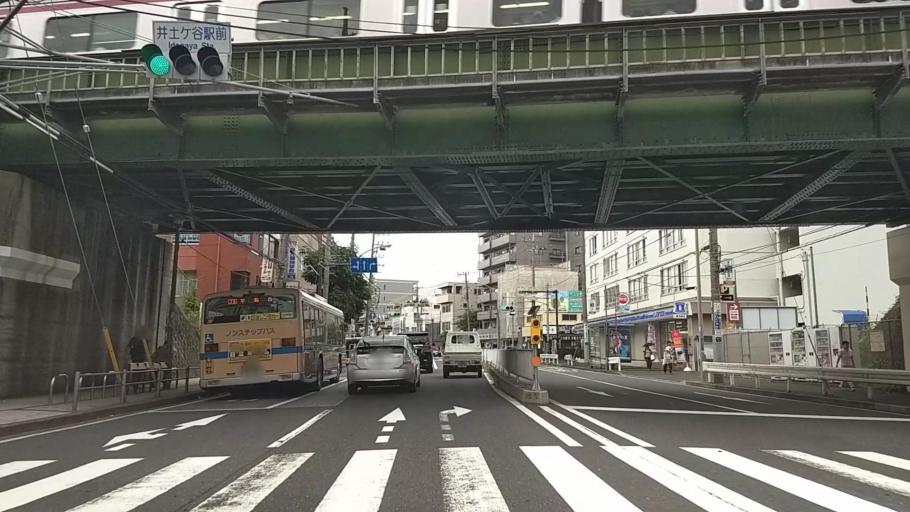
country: JP
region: Kanagawa
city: Yokohama
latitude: 35.4340
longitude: 139.6015
